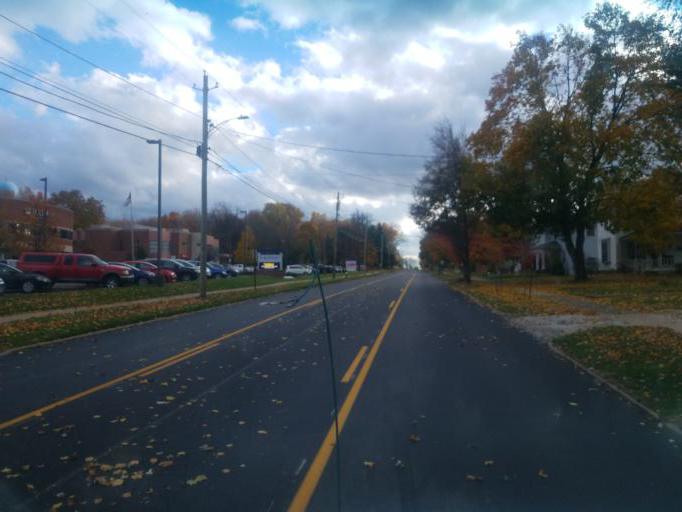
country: US
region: Ohio
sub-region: Wayne County
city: Orrville
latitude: 40.8325
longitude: -81.7646
